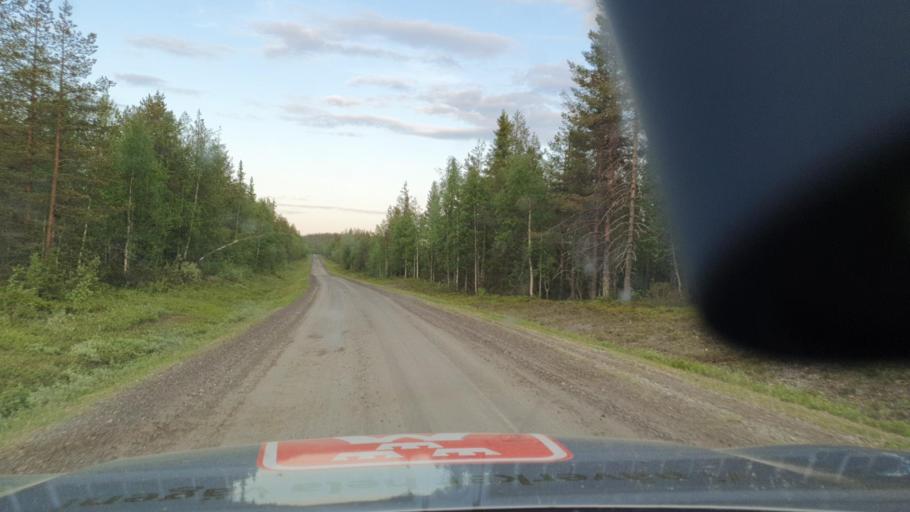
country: SE
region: Norrbotten
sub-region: Bodens Kommun
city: Boden
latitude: 66.5218
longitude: 21.5014
